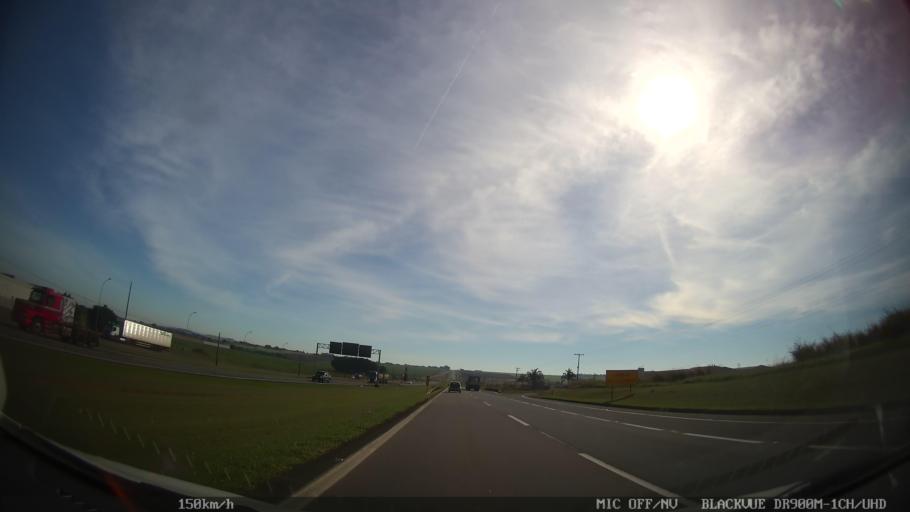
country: BR
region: Sao Paulo
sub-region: Cordeiropolis
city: Cordeiropolis
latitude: -22.4912
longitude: -47.3992
